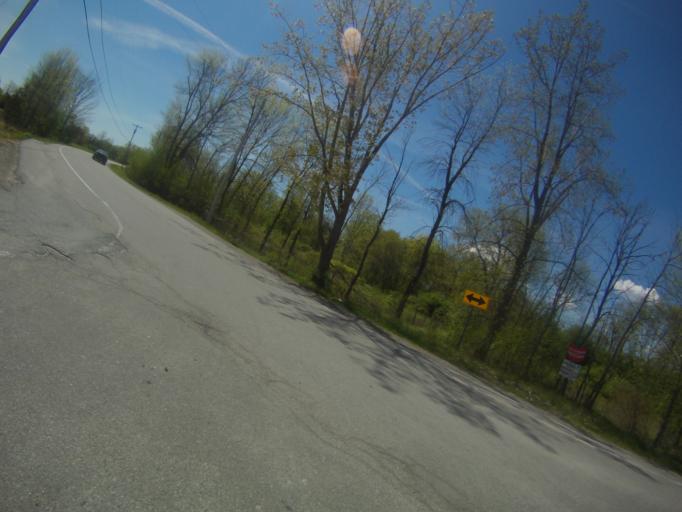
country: US
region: New York
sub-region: Essex County
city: Port Henry
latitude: 43.9857
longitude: -73.4251
